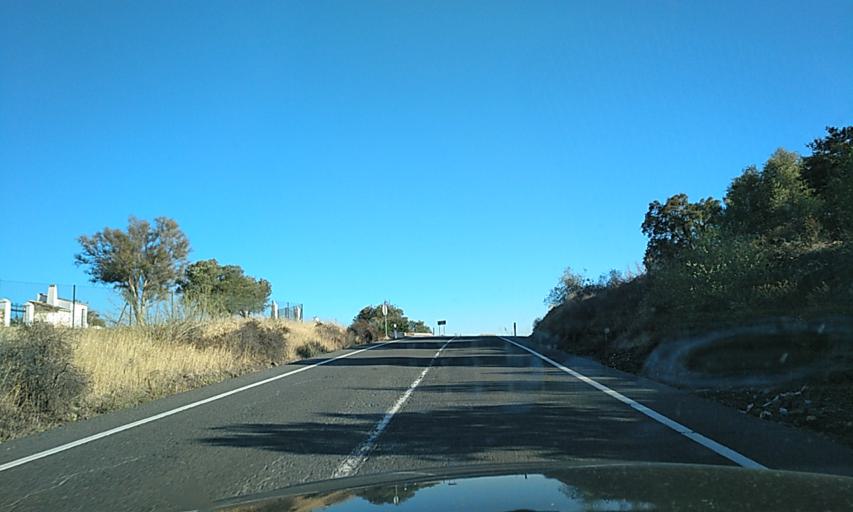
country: ES
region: Andalusia
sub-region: Provincia de Huelva
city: Alosno
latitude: 37.4987
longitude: -7.1319
